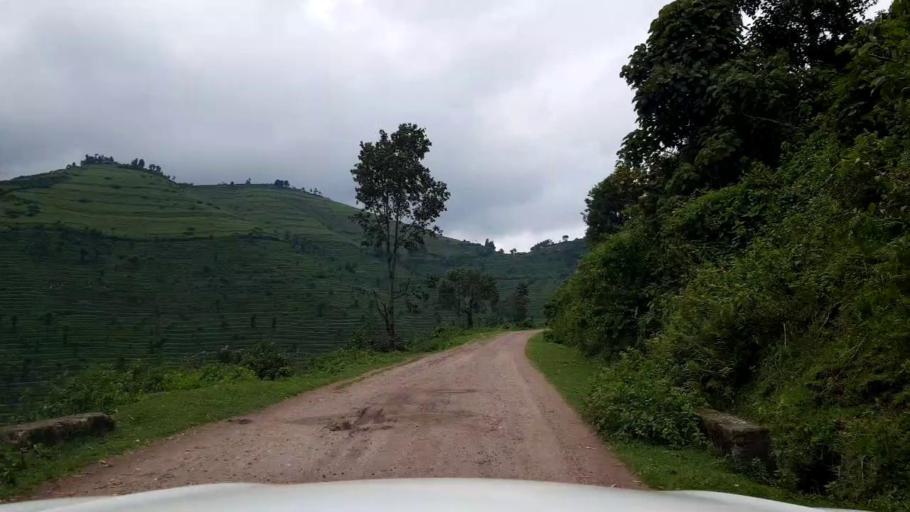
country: RW
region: Western Province
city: Gisenyi
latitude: -1.6657
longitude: 29.4176
